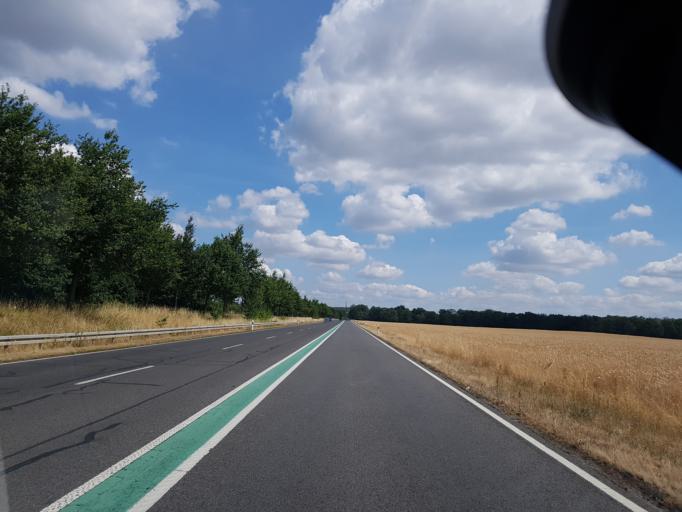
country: DE
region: Brandenburg
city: Drebkau
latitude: 51.6812
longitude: 14.2568
